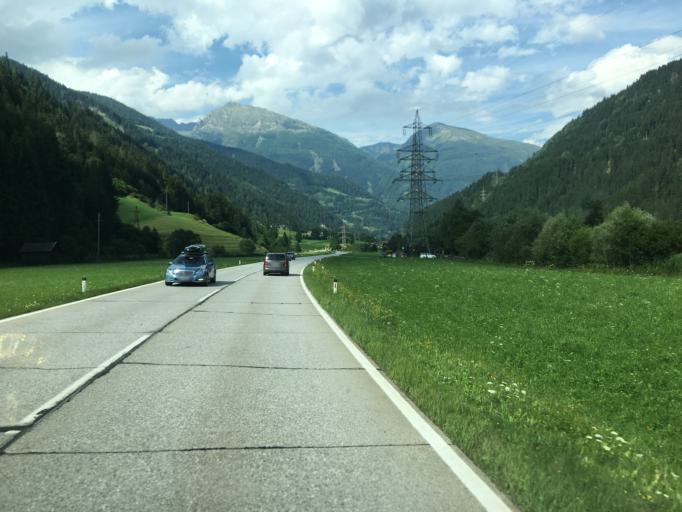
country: AT
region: Carinthia
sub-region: Politischer Bezirk Spittal an der Drau
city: Stall
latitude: 46.9092
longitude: 13.0667
